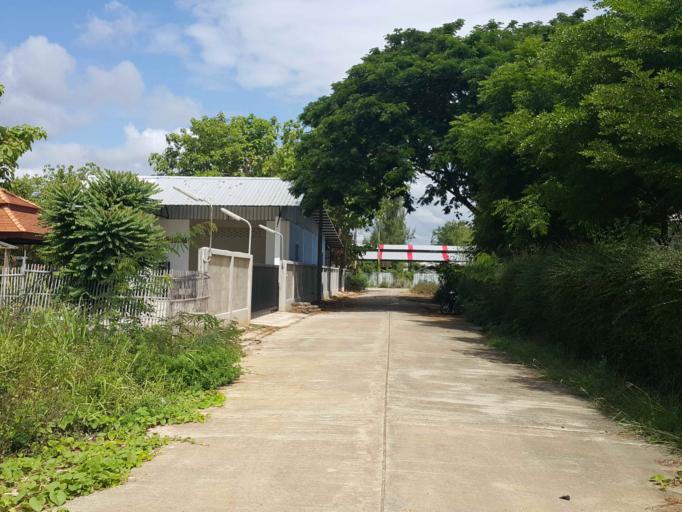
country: TH
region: Chiang Mai
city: Saraphi
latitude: 18.7200
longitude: 99.0499
